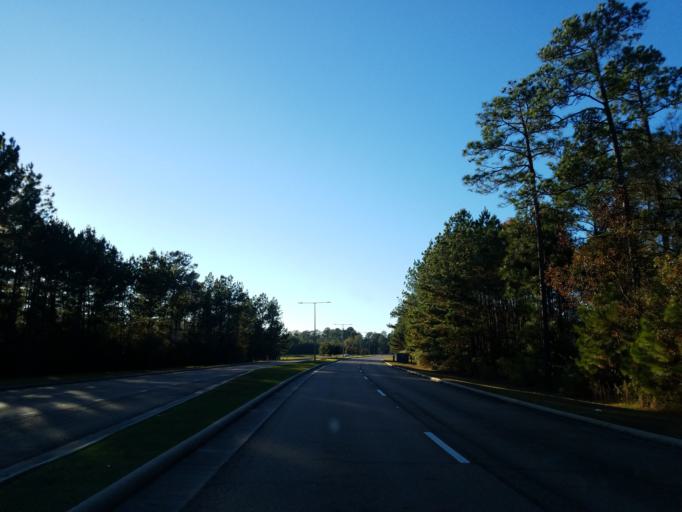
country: US
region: Mississippi
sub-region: Lamar County
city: Arnold Line
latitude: 31.3535
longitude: -89.3673
